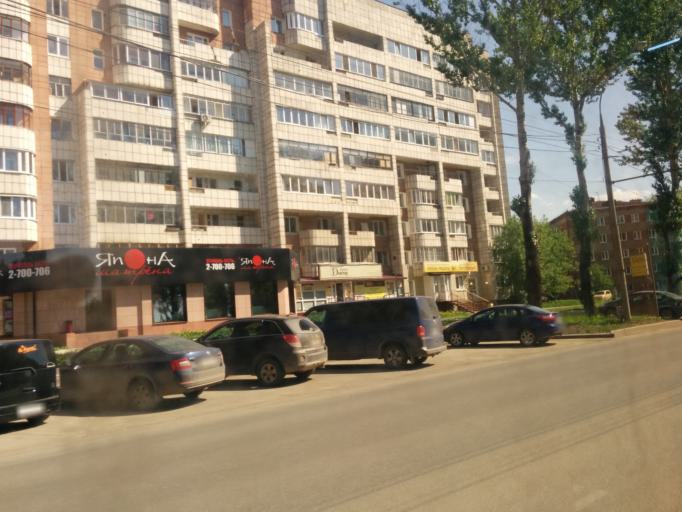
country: RU
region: Perm
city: Perm
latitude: 58.0134
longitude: 56.2807
